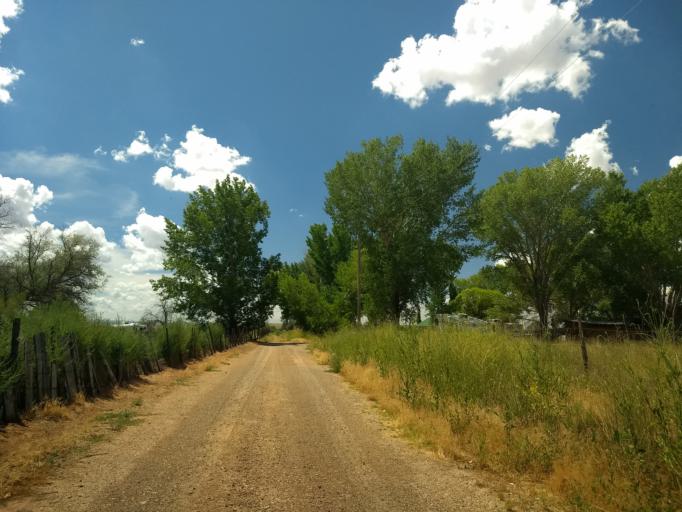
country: US
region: Arizona
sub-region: Coconino County
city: Fredonia
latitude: 36.9394
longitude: -112.5308
